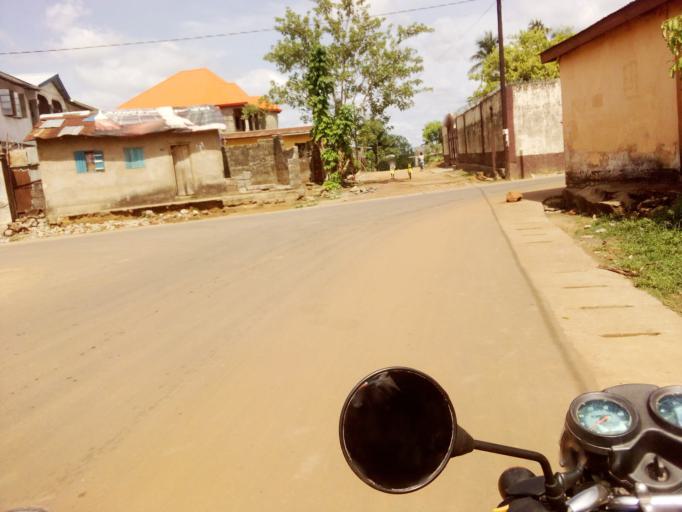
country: SL
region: Western Area
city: Waterloo
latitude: 8.3348
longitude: -13.0695
